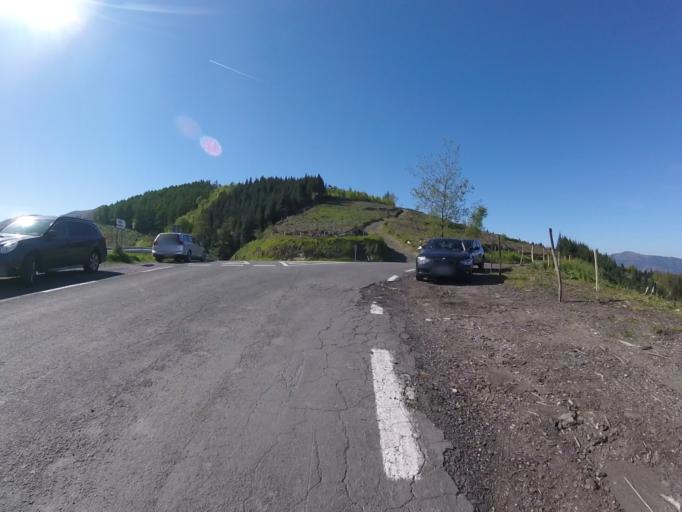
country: ES
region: Basque Country
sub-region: Provincia de Guipuzcoa
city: Errezil
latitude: 43.2028
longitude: -2.1976
